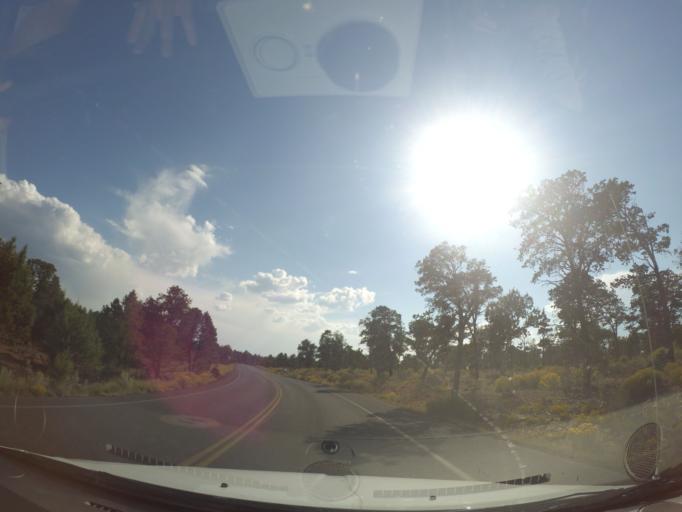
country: US
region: Arizona
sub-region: Coconino County
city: Grand Canyon
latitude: 36.0591
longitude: -112.1124
